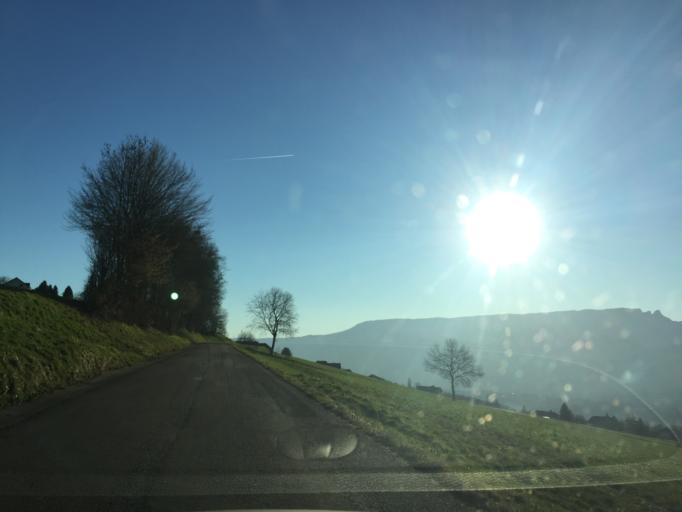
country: FR
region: Rhone-Alpes
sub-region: Departement de la Savoie
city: Mouxy
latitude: 45.7009
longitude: 5.9571
